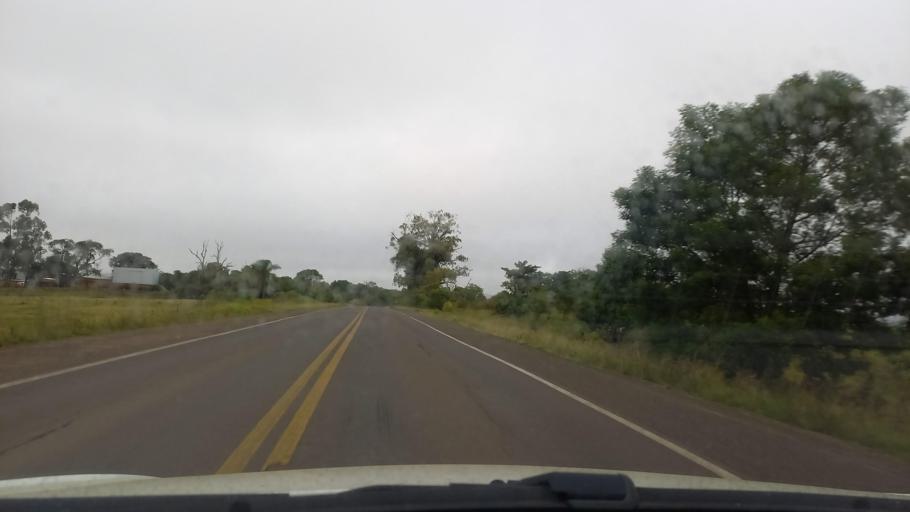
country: BR
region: Rio Grande do Sul
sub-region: Cacequi
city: Cacequi
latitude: -30.0950
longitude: -54.6295
